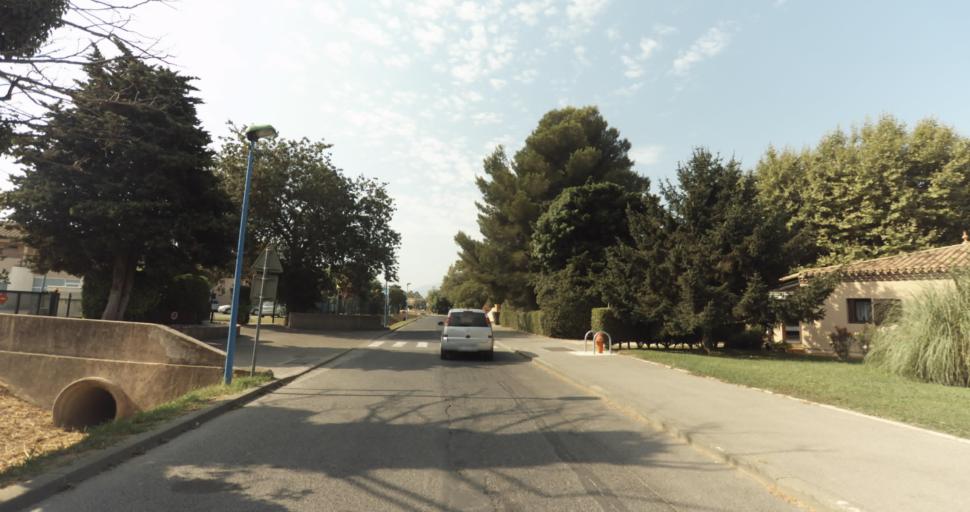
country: FR
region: Languedoc-Roussillon
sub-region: Departement des Pyrenees-Orientales
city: Saint-Cyprien-Plage
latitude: 42.6068
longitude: 3.0316
